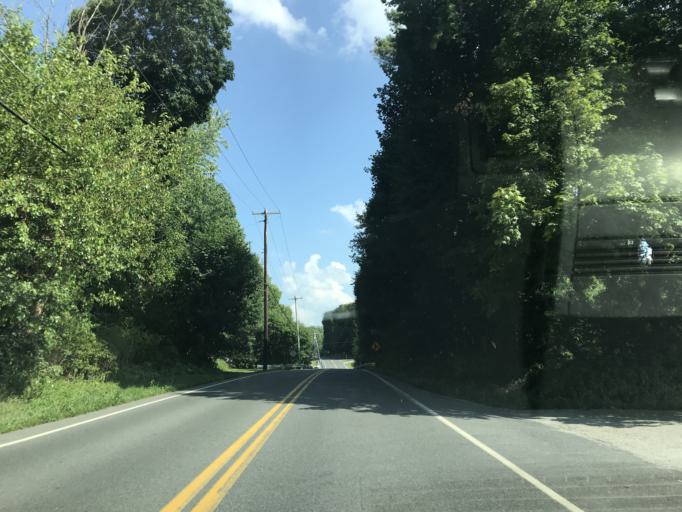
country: US
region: Pennsylvania
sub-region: York County
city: Glen Rock
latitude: 39.7587
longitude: -76.8155
